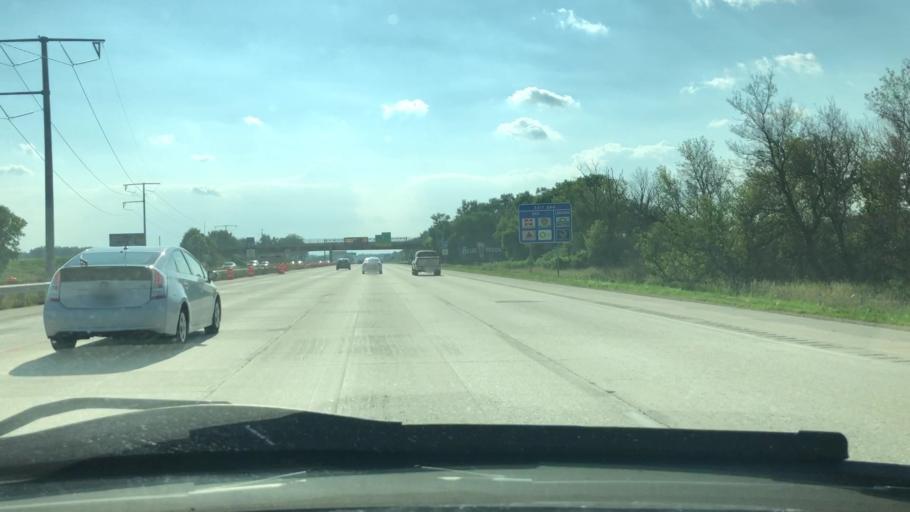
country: US
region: Wisconsin
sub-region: Dane County
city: McFarland
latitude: 43.0479
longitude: -89.2871
